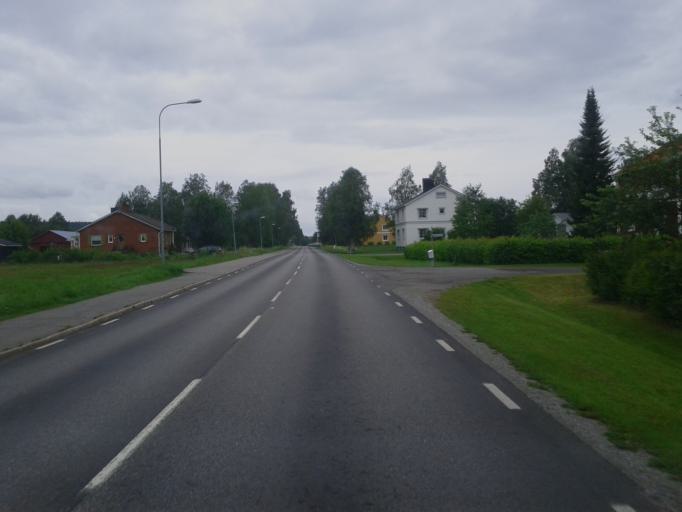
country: SE
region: Vaesterbotten
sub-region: Skelleftea Kommun
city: Kage
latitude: 64.8782
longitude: 20.7982
